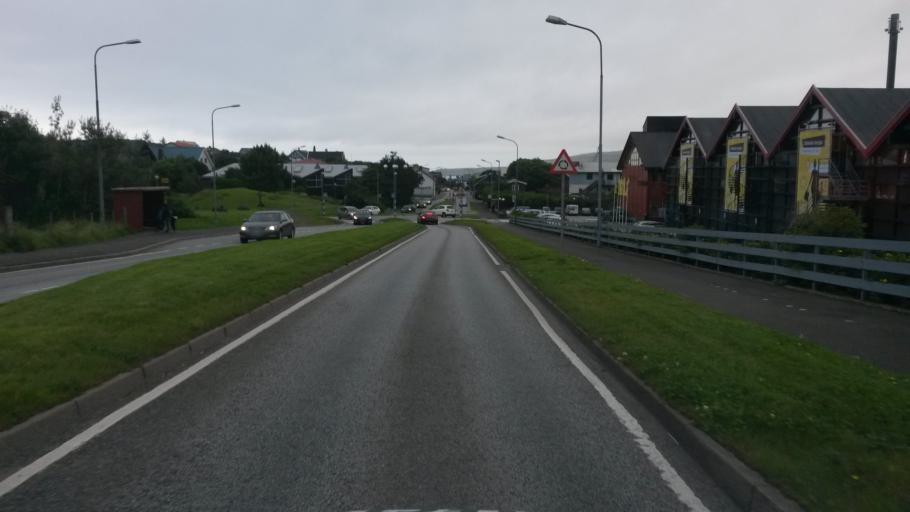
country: FO
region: Streymoy
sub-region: Torshavn
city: Torshavn
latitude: 62.0149
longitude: -6.7739
